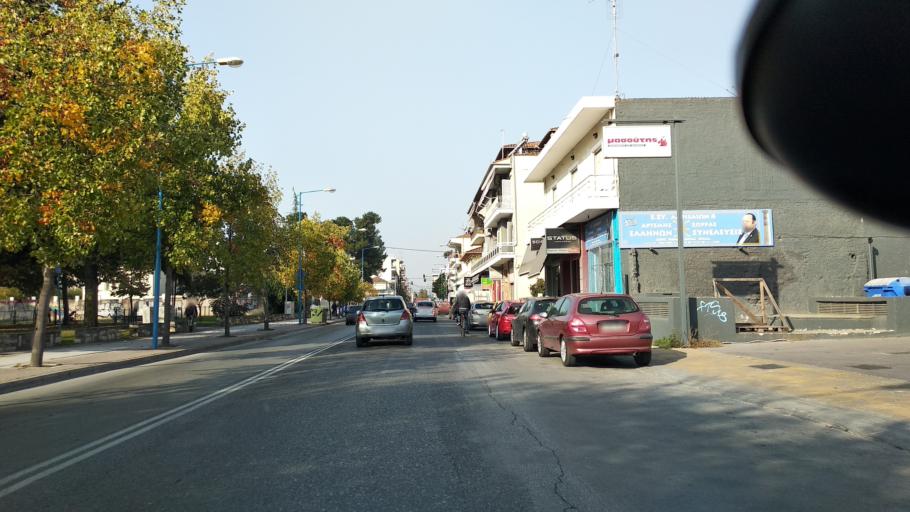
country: GR
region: Thessaly
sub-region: Nomos Larisis
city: Larisa
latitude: 39.6327
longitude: 22.4007
